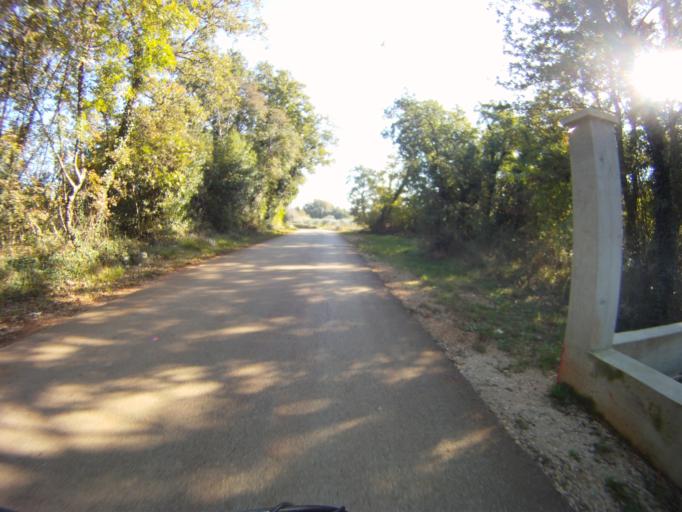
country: HR
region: Istarska
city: Umag
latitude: 45.3963
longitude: 13.5360
